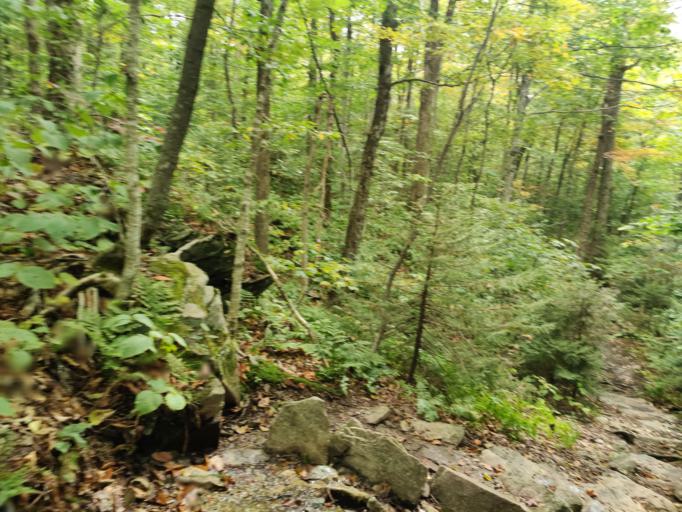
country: US
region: Vermont
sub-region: Bennington County
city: Manchester Center
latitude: 43.2621
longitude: -72.9403
